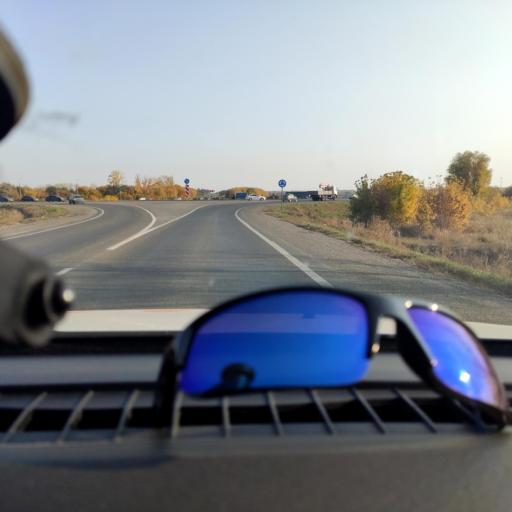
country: RU
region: Samara
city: Samara
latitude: 53.0934
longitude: 50.1495
